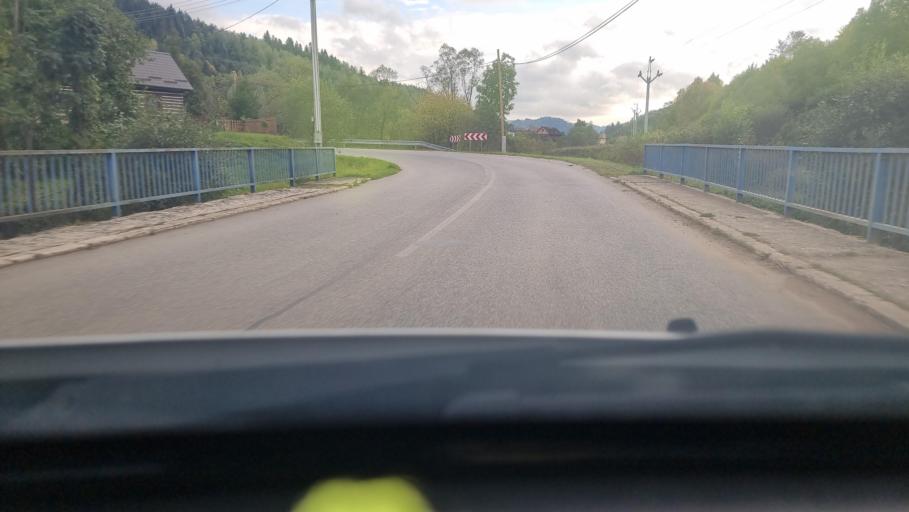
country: PL
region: Lesser Poland Voivodeship
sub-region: Powiat nowotarski
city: Szczawnica
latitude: 49.3604
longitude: 20.4462
